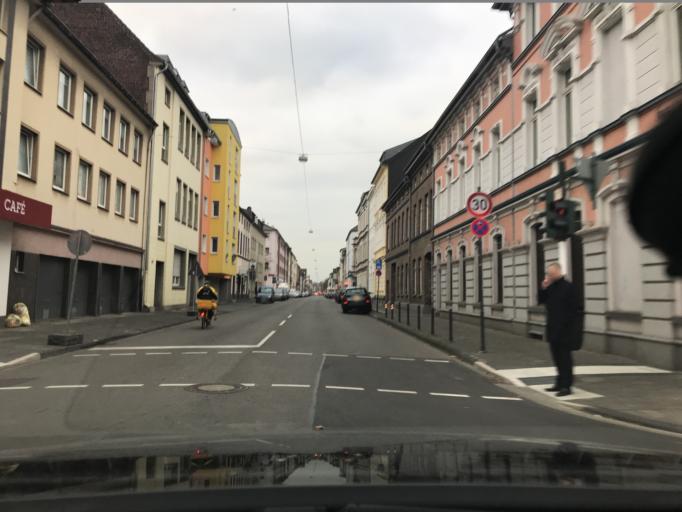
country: DE
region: North Rhine-Westphalia
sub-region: Regierungsbezirk Dusseldorf
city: Krefeld
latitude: 51.3295
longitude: 6.5581
